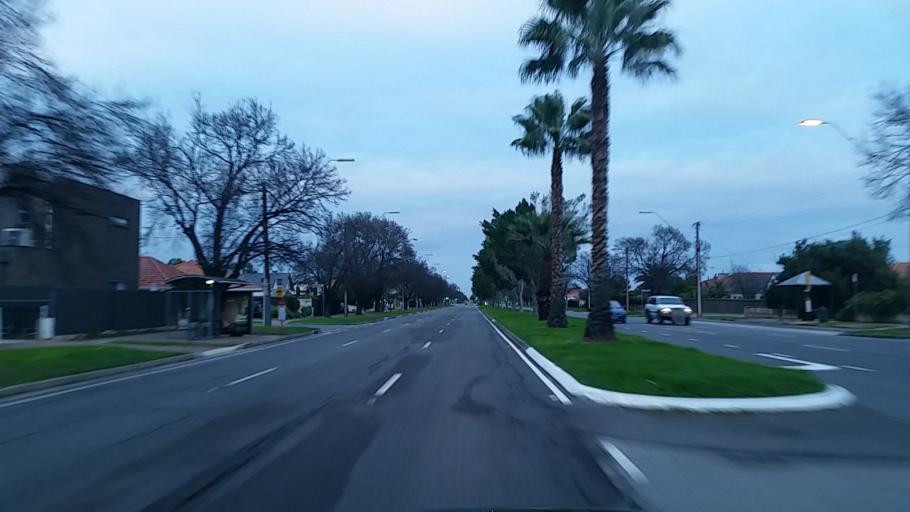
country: AU
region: South Australia
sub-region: Marion
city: South Plympton
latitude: -34.9655
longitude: 138.5525
